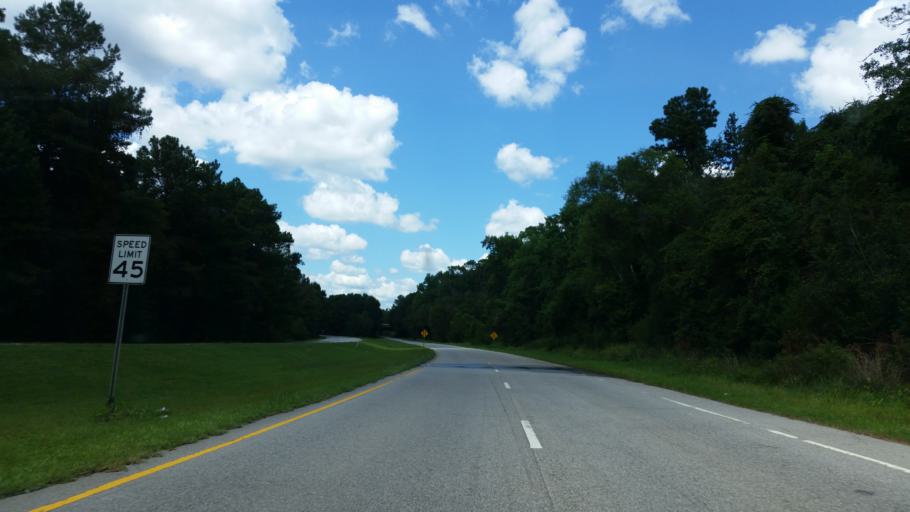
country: US
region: Alabama
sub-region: Baldwin County
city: Spanish Fort
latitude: 30.6624
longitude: -87.9137
